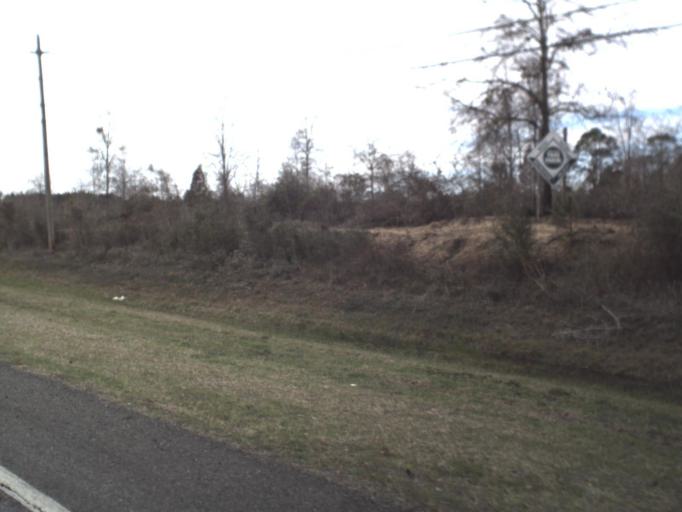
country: US
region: Florida
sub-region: Bay County
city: Youngstown
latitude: 30.3146
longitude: -85.4643
